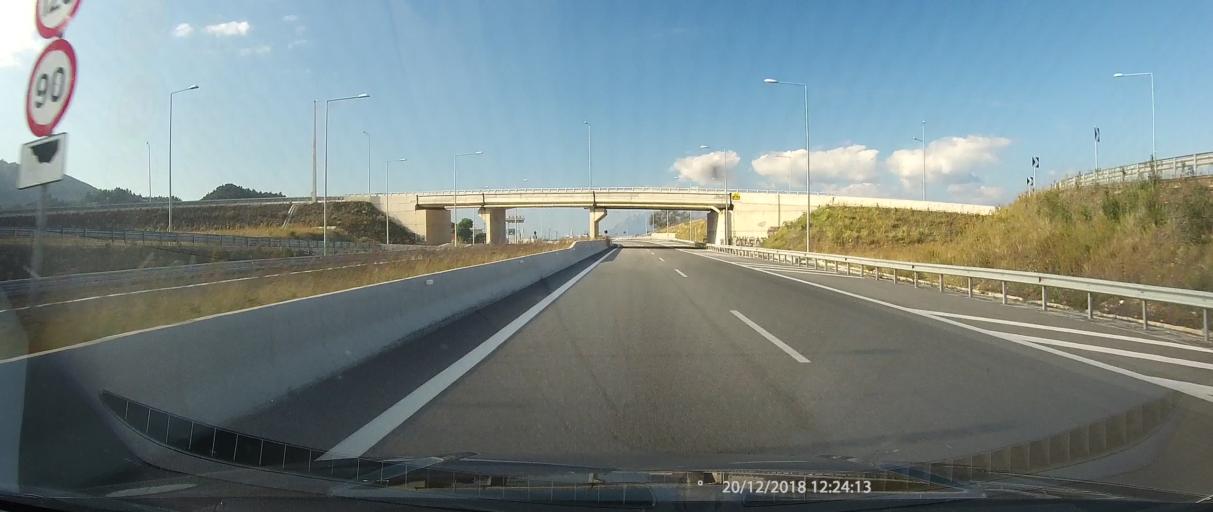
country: GR
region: West Greece
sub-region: Nomos Achaias
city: Ano Kastritsion
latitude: 38.3242
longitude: 21.8567
